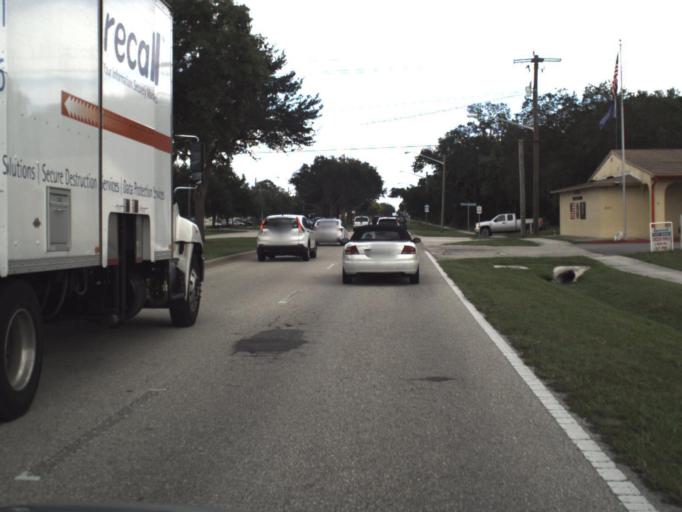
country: US
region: Florida
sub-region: Sarasota County
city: Venice
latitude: 27.0997
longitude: -82.4303
